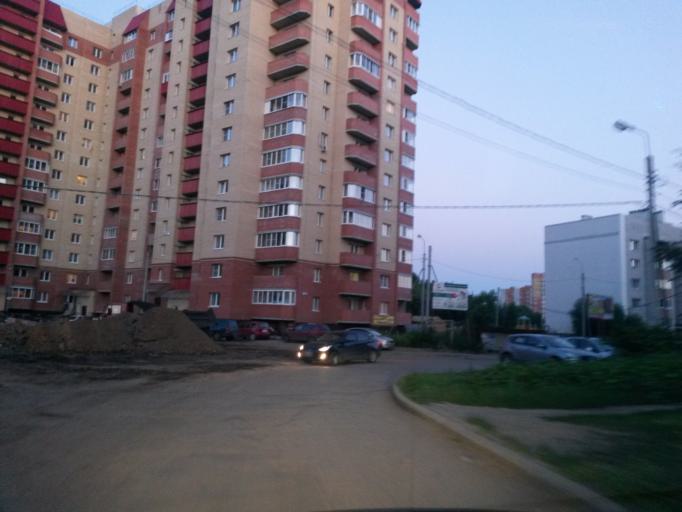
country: RU
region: Jaroslavl
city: Yaroslavl
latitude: 57.6964
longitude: 39.7821
